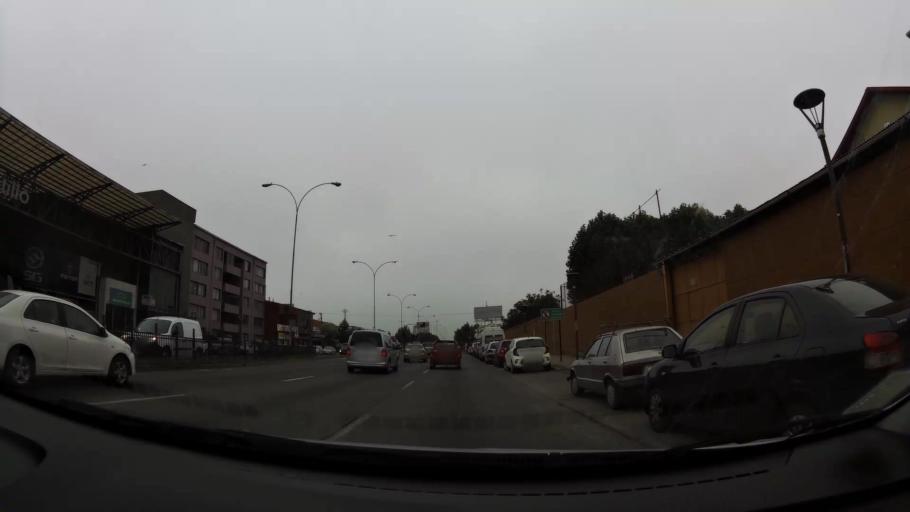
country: CL
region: Biobio
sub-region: Provincia de Concepcion
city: Concepcion
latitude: -36.8253
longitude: -73.0565
